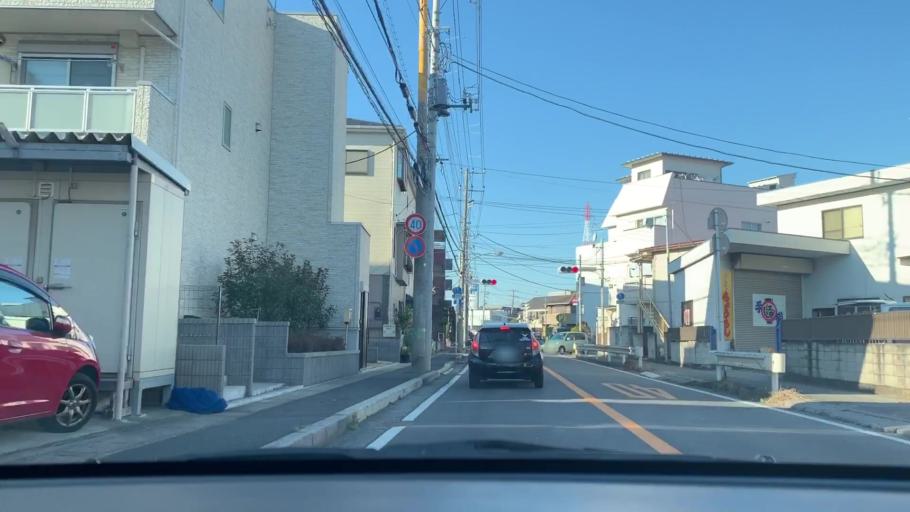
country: JP
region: Chiba
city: Matsudo
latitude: 35.7264
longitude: 139.9013
